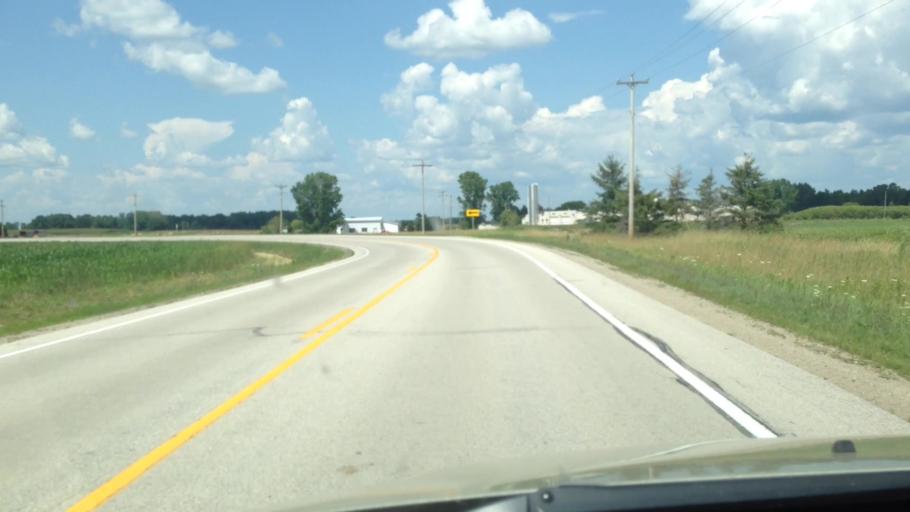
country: US
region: Wisconsin
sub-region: Brown County
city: Pulaski
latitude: 44.6566
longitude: -88.1809
